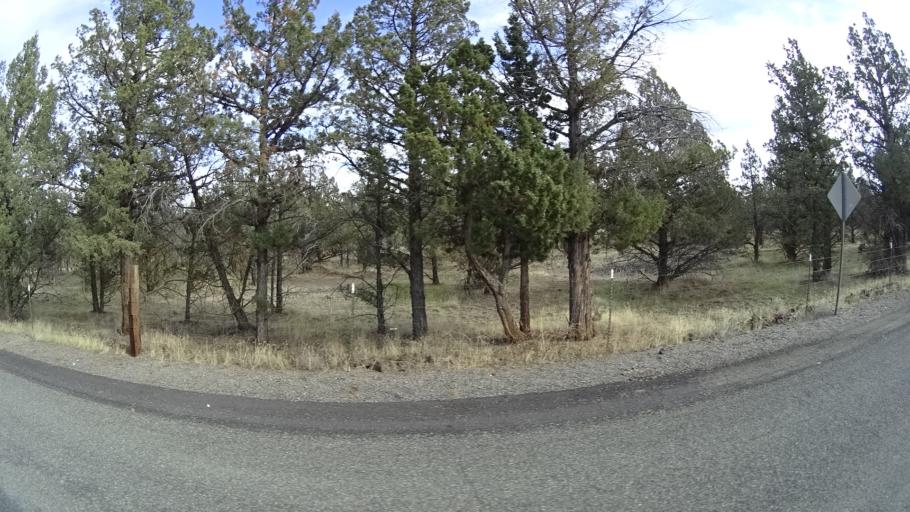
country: US
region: California
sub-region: Siskiyou County
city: Montague
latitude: 41.6469
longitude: -122.4189
